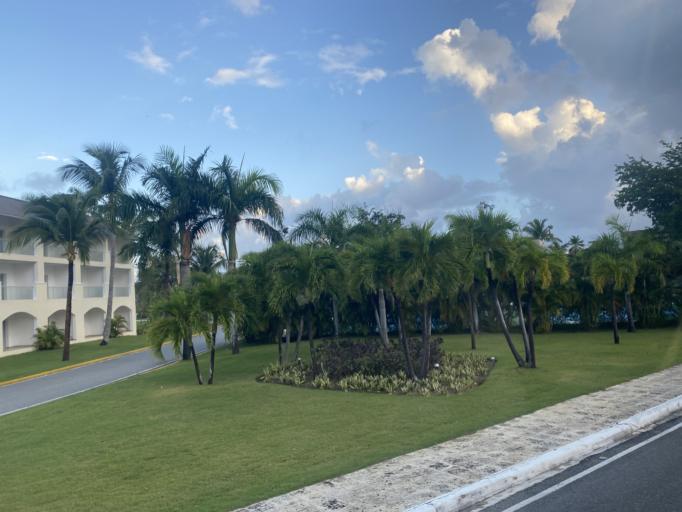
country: DO
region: San Juan
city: Punta Cana
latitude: 18.7269
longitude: -68.4708
